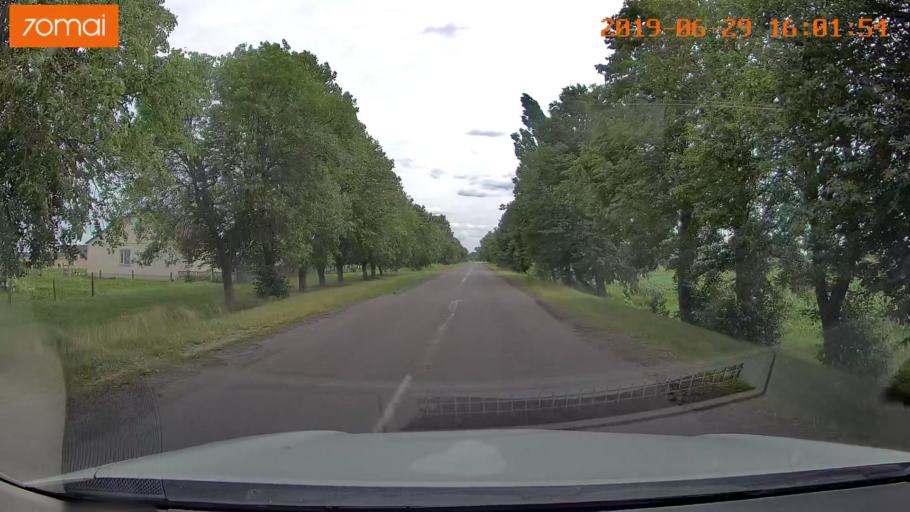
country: BY
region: Brest
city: Luninyets
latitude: 52.2415
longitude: 27.0160
